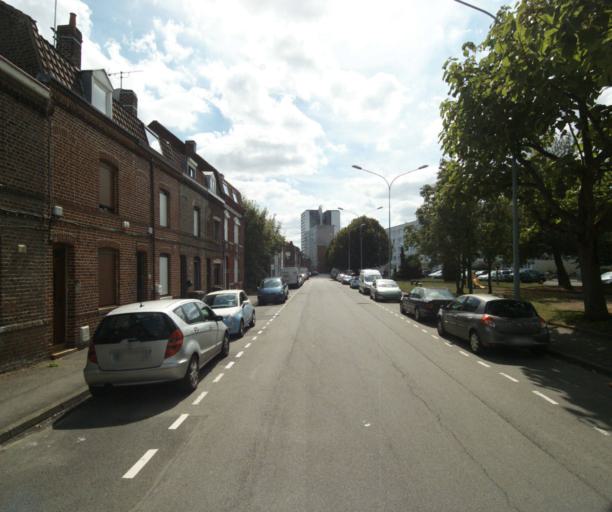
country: FR
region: Nord-Pas-de-Calais
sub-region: Departement du Nord
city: Mons-en-Baroeul
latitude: 50.6401
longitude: 3.1122
